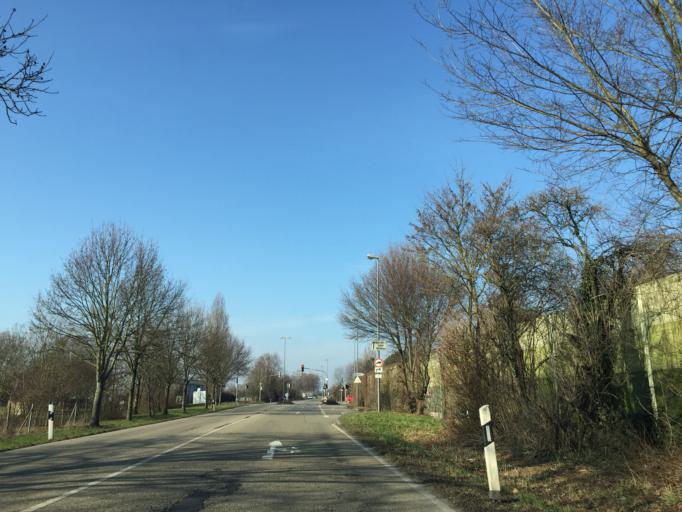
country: DE
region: Baden-Wuerttemberg
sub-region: Karlsruhe Region
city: Eppelheim
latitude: 49.4203
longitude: 8.6415
